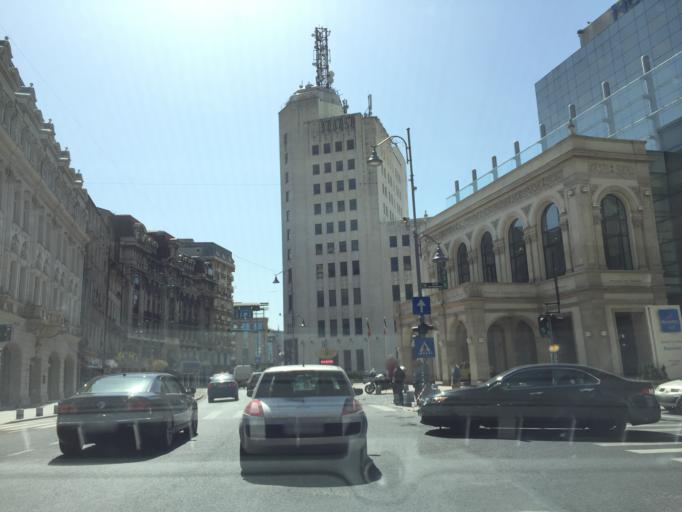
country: RO
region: Bucuresti
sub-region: Municipiul Bucuresti
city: Bucuresti
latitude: 44.4373
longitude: 26.0975
